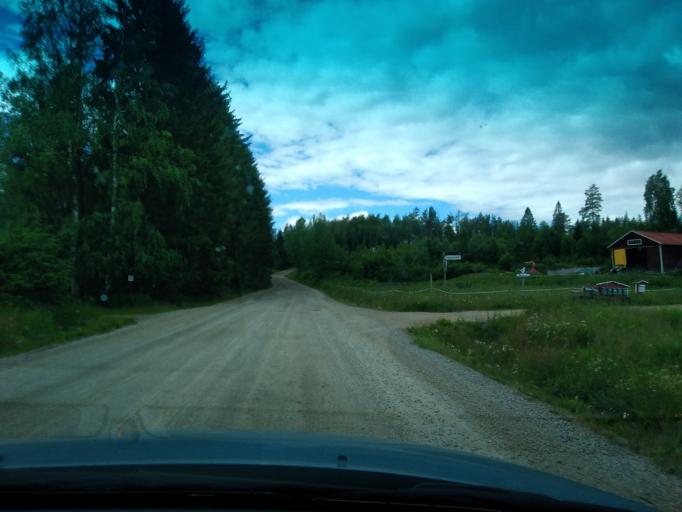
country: FI
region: Central Finland
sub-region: Saarijaervi-Viitasaari
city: Karstula
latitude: 62.8097
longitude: 25.0209
